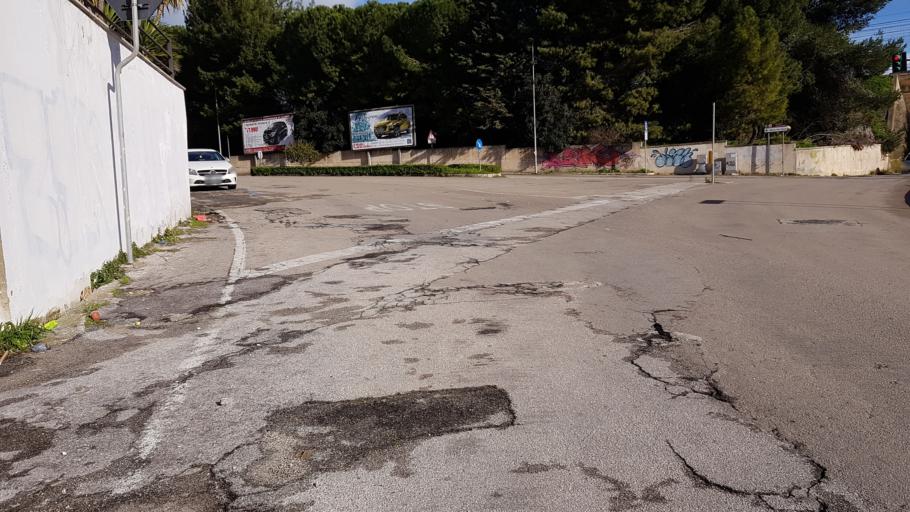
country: IT
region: Apulia
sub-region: Provincia di Brindisi
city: Brindisi
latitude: 40.6294
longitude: 17.9413
